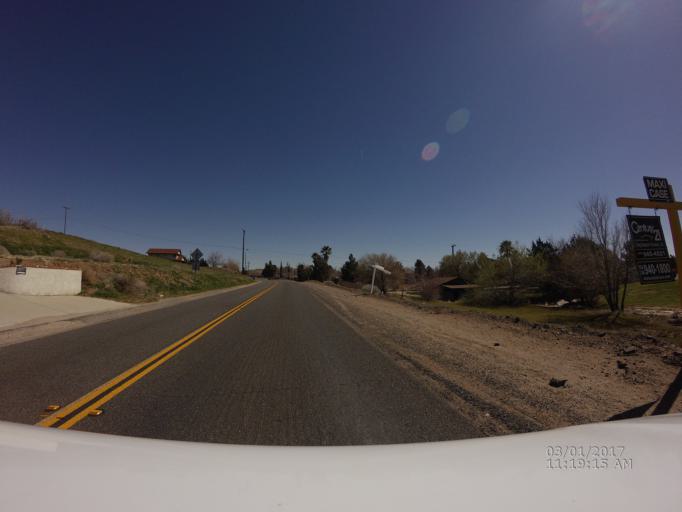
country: US
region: California
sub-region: Los Angeles County
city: Quartz Hill
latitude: 34.6437
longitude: -118.2137
